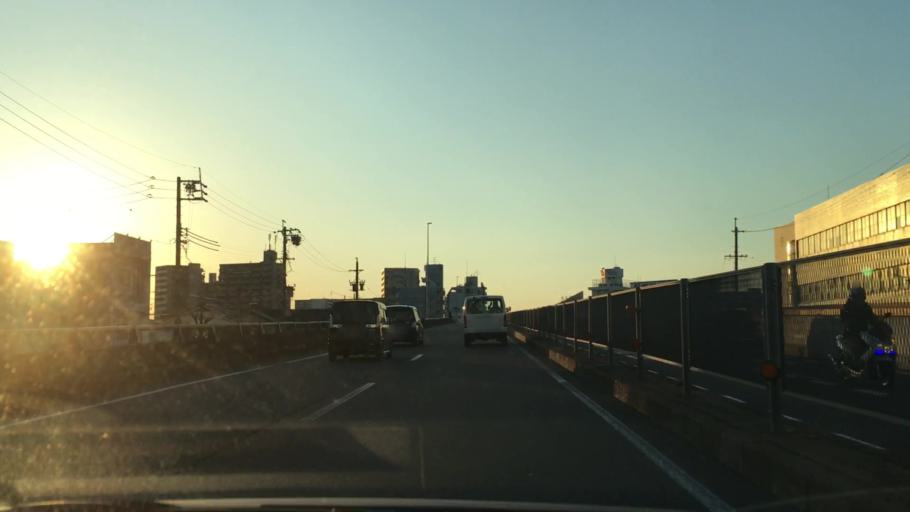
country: JP
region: Aichi
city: Nagoya-shi
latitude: 35.1168
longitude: 136.9170
